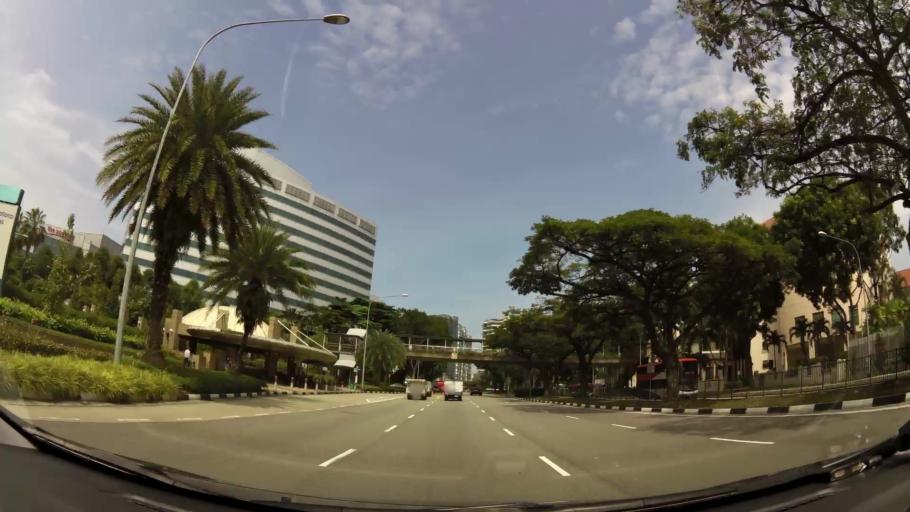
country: SG
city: Singapore
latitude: 1.3300
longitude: 103.7485
